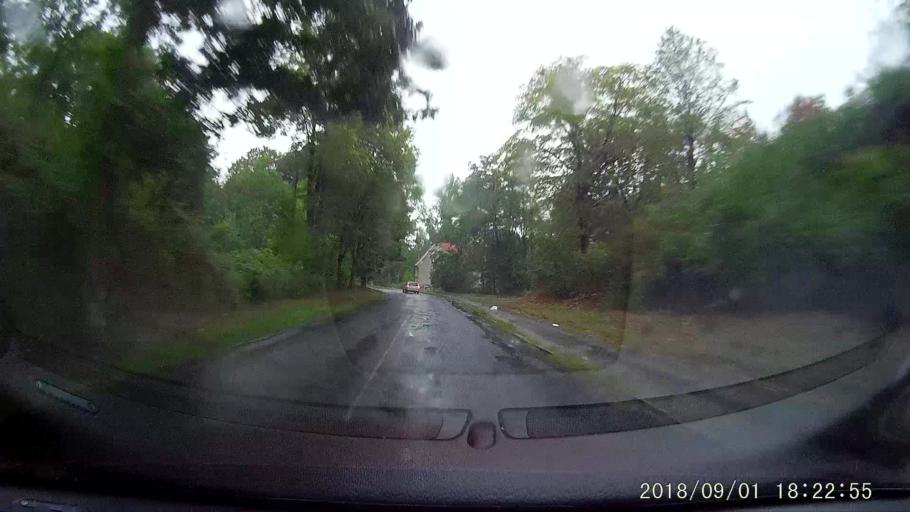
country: PL
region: Lower Silesian Voivodeship
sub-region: Powiat zgorzelecki
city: Piensk
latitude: 51.2470
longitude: 15.0407
